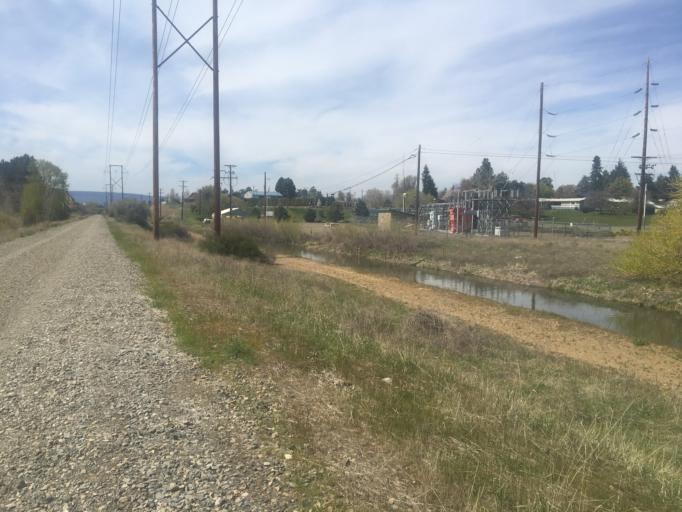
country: US
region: Washington
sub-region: Kittitas County
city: Ellensburg
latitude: 46.9992
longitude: -120.5214
